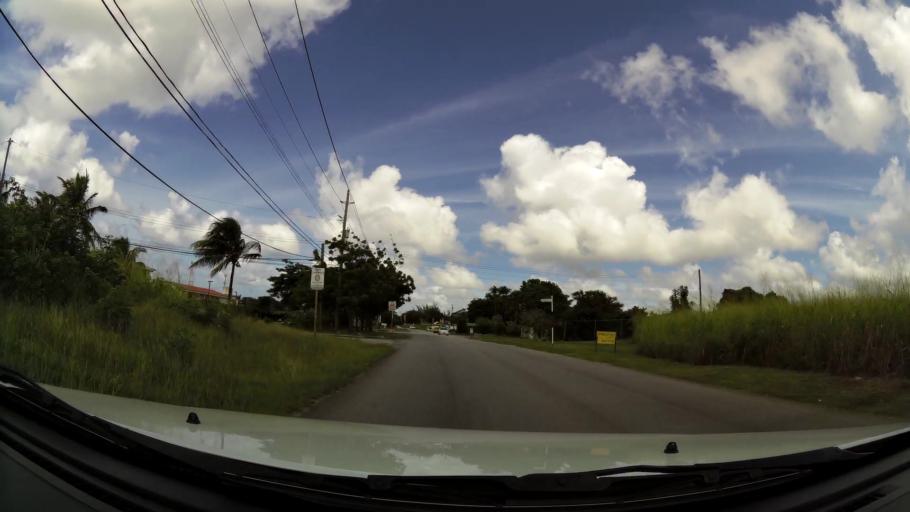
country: BB
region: Saint James
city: Holetown
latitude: 13.1448
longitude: -59.6227
